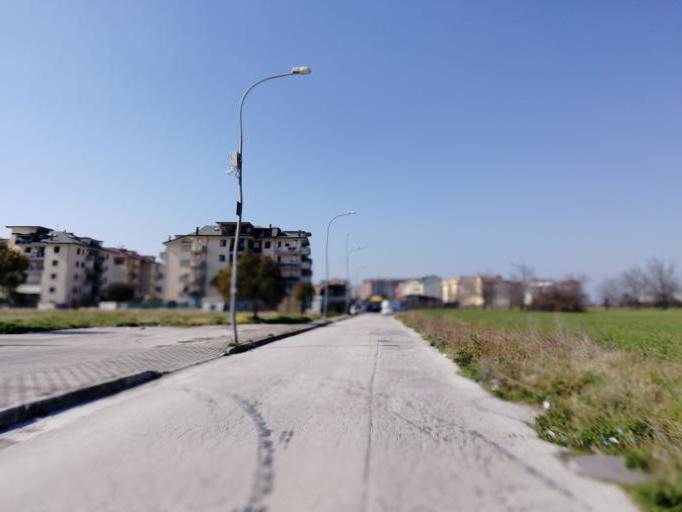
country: IT
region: Campania
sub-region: Provincia di Caserta
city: San Prisco
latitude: 41.0897
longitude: 14.2708
